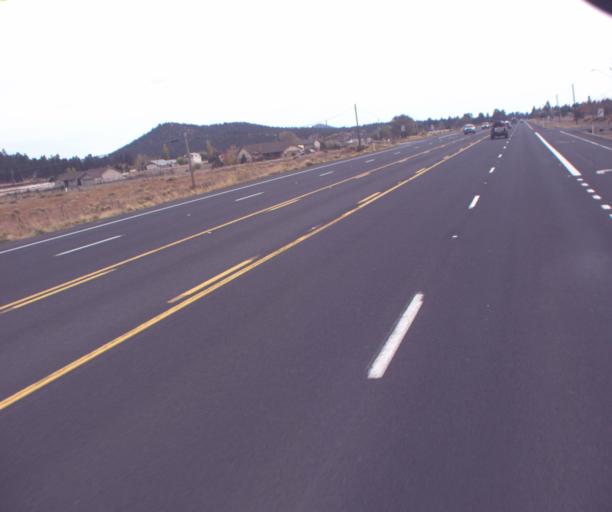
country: US
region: Arizona
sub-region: Coconino County
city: Flagstaff
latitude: 35.2996
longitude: -111.5428
